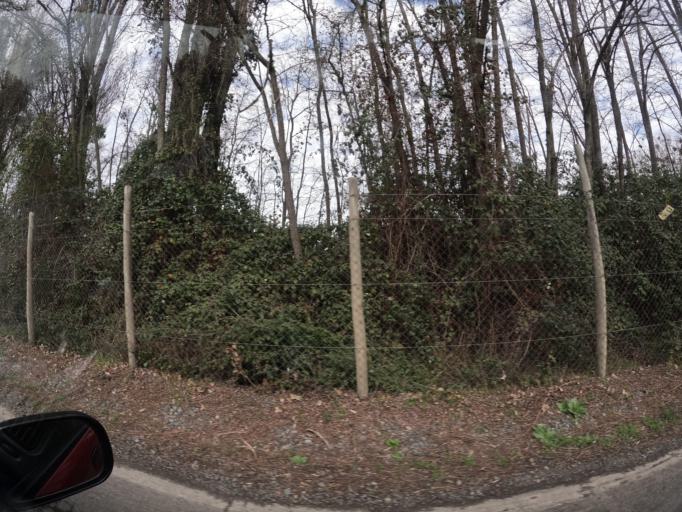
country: CL
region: Maule
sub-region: Provincia de Linares
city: Linares
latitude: -35.8662
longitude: -71.6265
